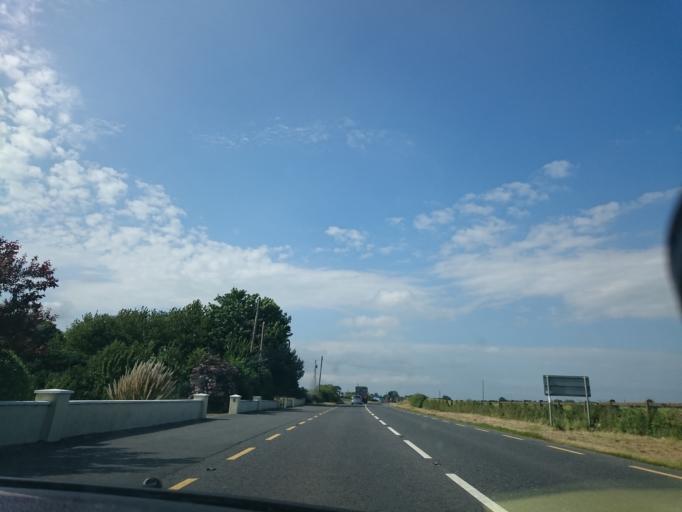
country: IE
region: Leinster
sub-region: Kilkenny
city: Kilkenny
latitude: 52.5850
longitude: -7.2399
